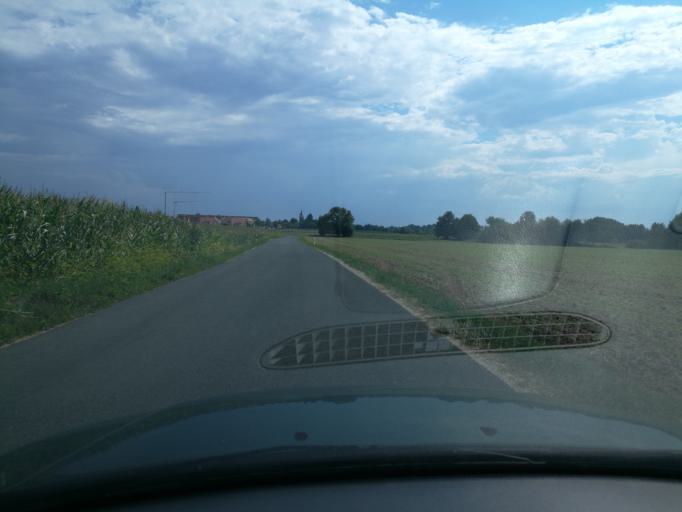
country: DE
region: Bavaria
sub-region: Regierungsbezirk Mittelfranken
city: Erlangen
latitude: 49.5397
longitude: 11.0133
